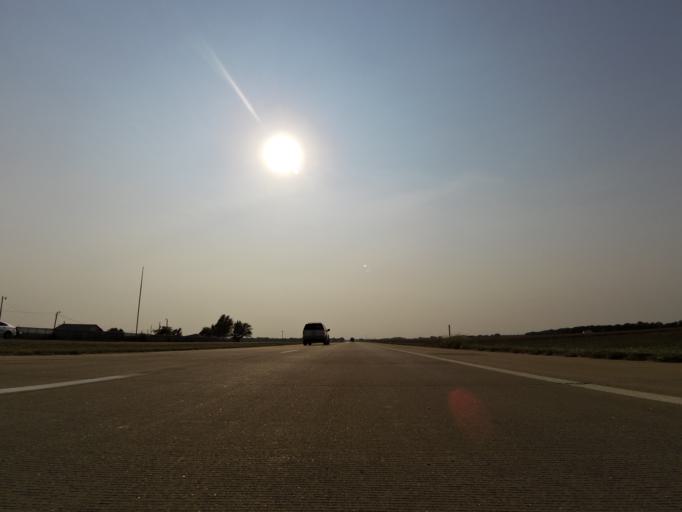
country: US
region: Kansas
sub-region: Sedgwick County
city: Colwich
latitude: 37.8761
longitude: -97.6399
